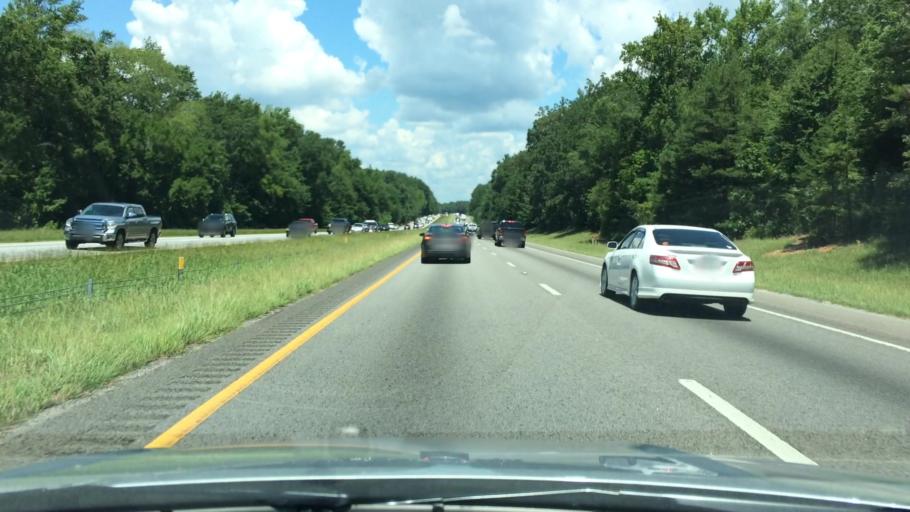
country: US
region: South Carolina
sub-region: Lexington County
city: Irmo
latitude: 34.1236
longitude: -81.2002
